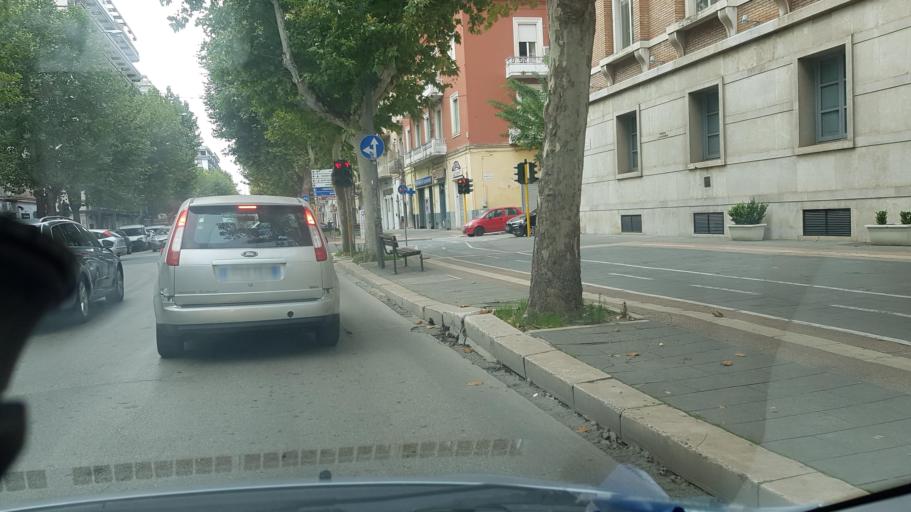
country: IT
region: Apulia
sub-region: Provincia di Foggia
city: Foggia
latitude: 41.4593
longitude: 15.5533
